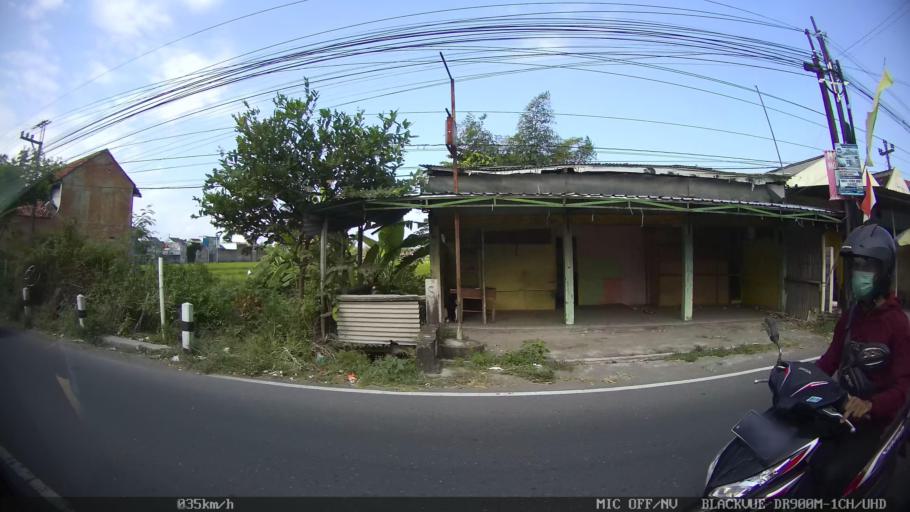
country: ID
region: Daerah Istimewa Yogyakarta
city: Sewon
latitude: -7.8516
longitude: 110.3904
